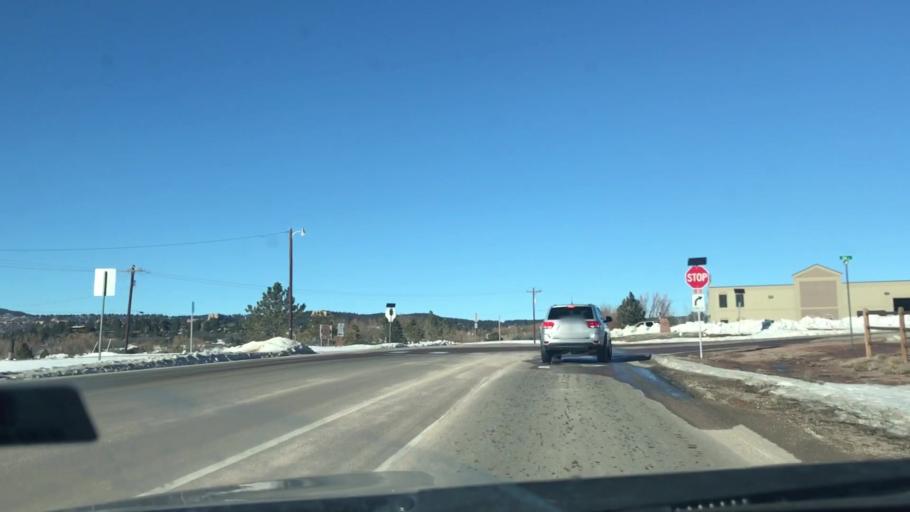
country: US
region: Colorado
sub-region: El Paso County
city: Monument
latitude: 39.0911
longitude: -104.8758
